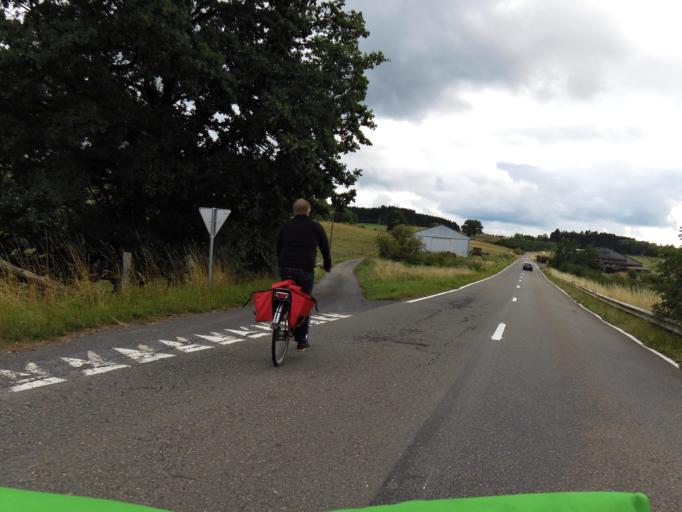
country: BE
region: Wallonia
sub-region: Province de Namur
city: Bievre
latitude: 49.8902
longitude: 5.0054
